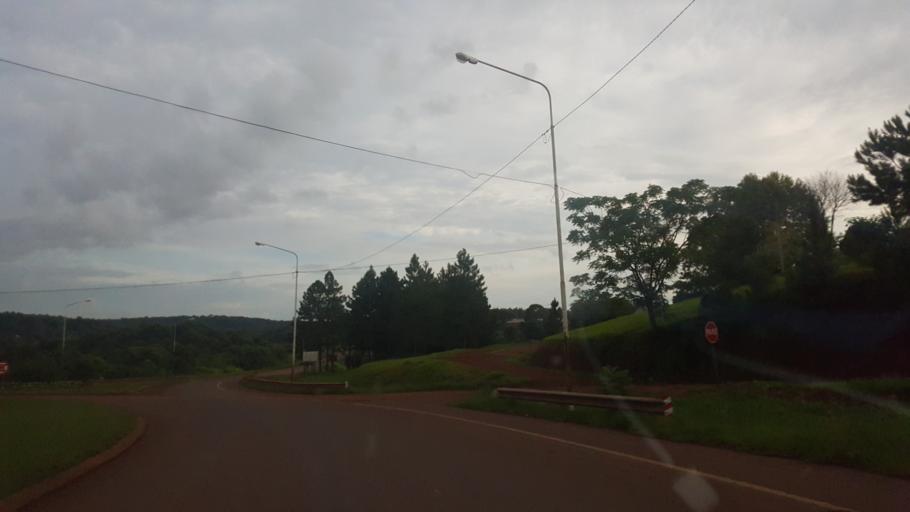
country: AR
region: Misiones
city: Dos de Mayo
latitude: -27.0364
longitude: -54.6753
